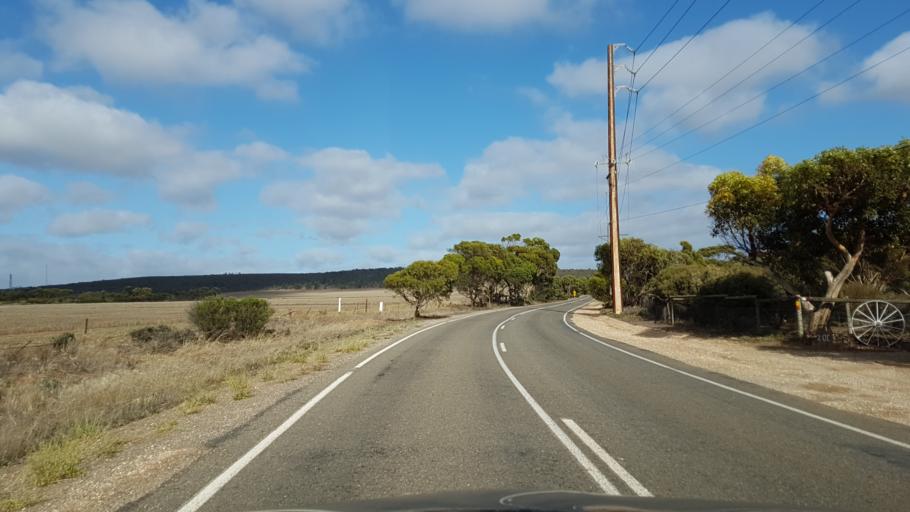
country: AU
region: South Australia
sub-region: Murray Bridge
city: Murray Bridge
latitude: -35.1178
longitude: 139.2407
